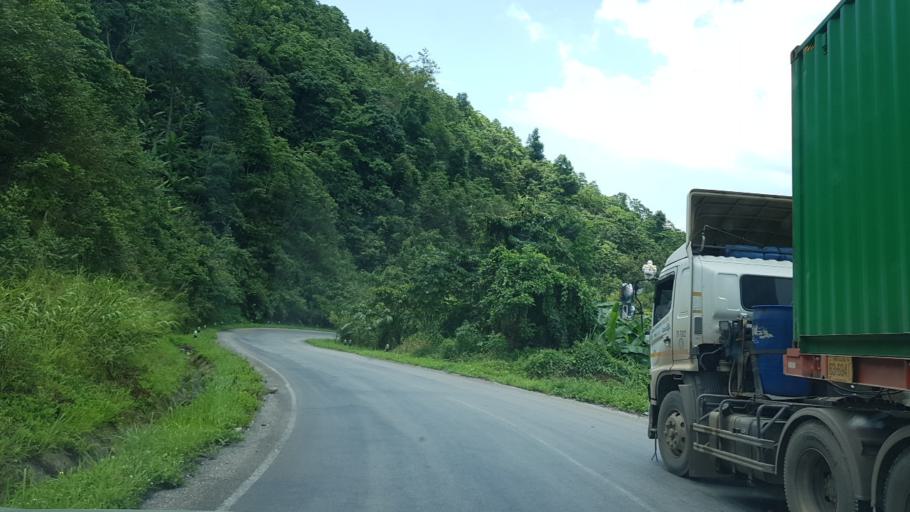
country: LA
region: Vientiane
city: Muang Kasi
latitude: 19.3711
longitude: 102.1602
